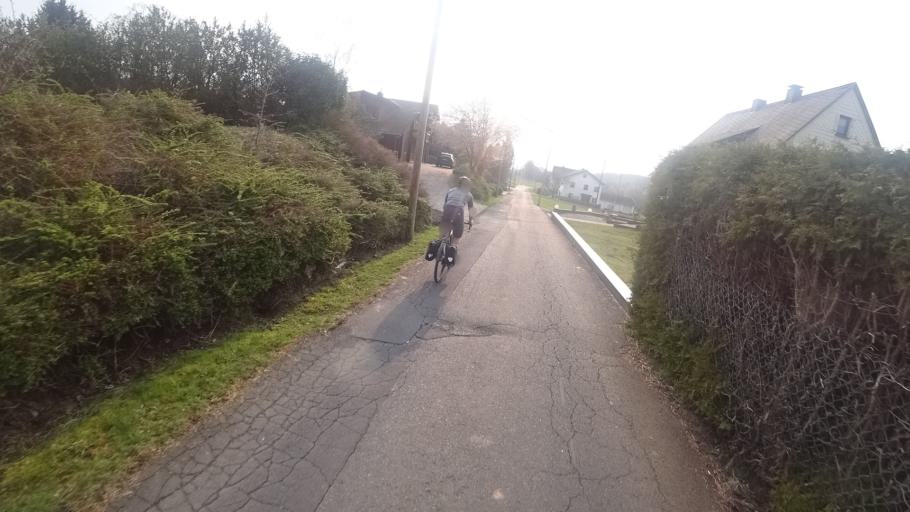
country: DE
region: Rheinland-Pfalz
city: Luckenbach
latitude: 50.7104
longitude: 7.8496
